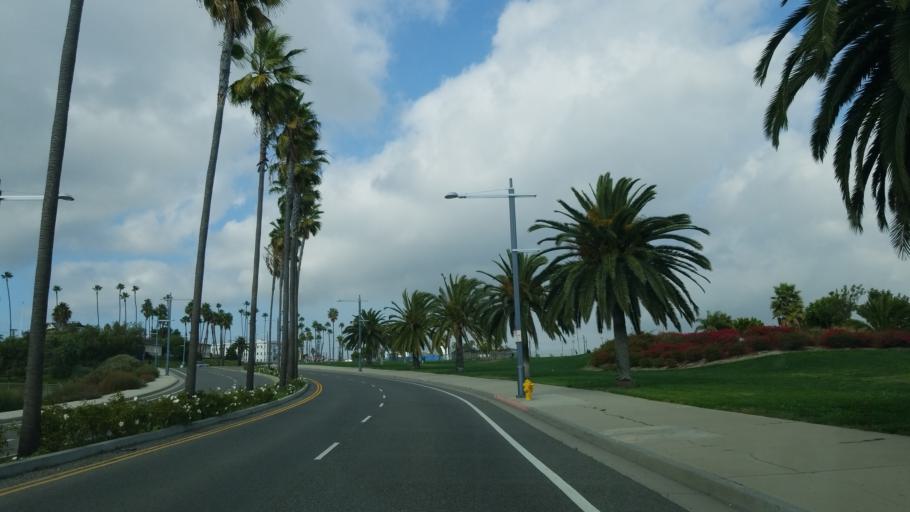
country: US
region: California
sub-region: Los Angeles County
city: San Pedro
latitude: 33.7280
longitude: -118.2787
